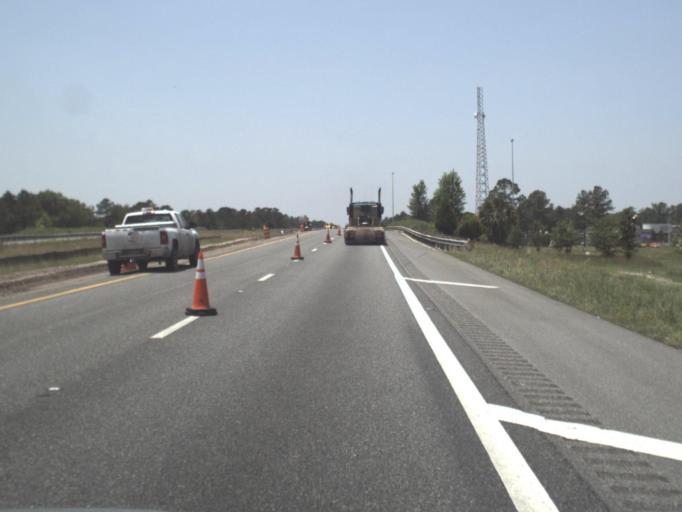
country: US
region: Florida
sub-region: Baker County
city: Macclenny
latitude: 30.2641
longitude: -82.1019
